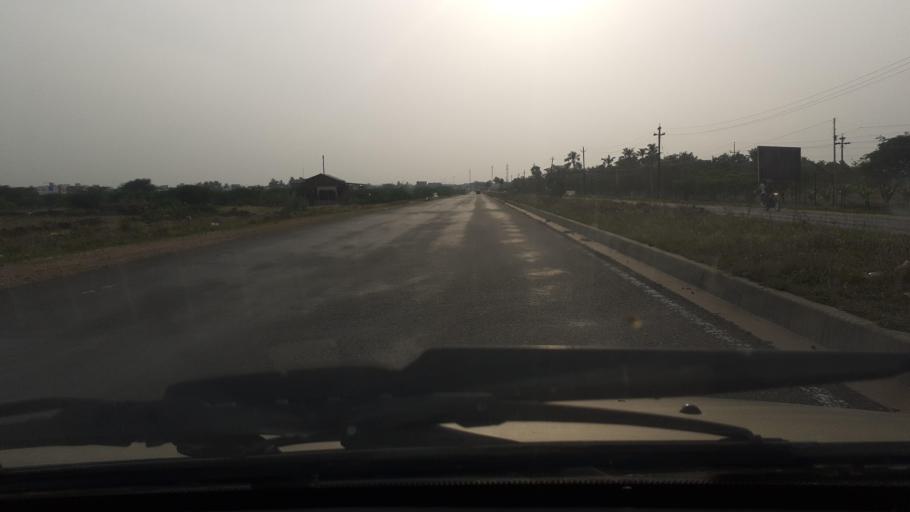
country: IN
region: Tamil Nadu
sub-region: Tirunelveli Kattabo
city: Tirunelveli
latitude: 8.7122
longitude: 77.7992
